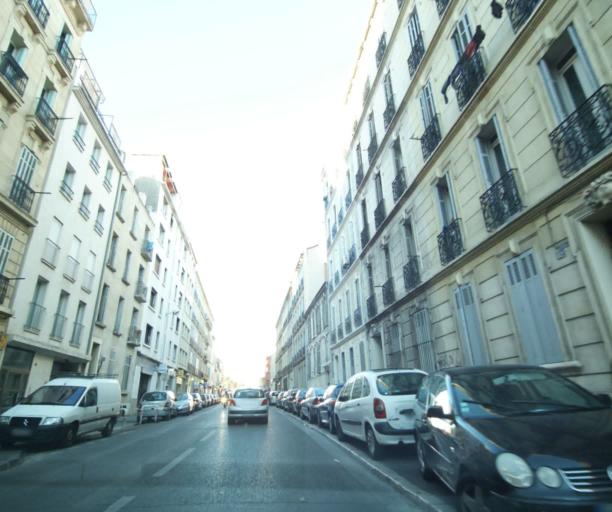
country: FR
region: Provence-Alpes-Cote d'Azur
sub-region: Departement des Bouches-du-Rhone
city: Marseille 04
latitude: 43.3088
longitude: 5.4004
